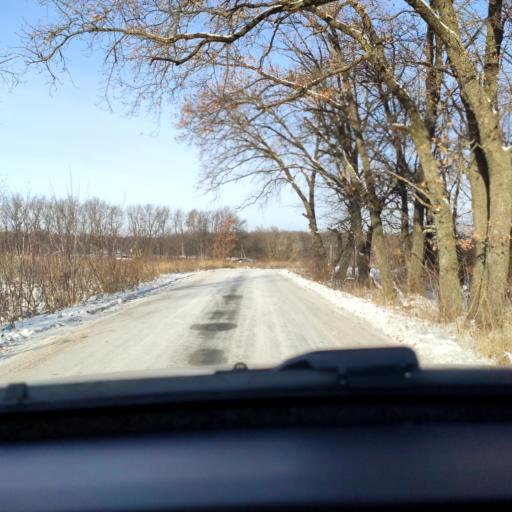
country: RU
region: Voronezj
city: Devitsa
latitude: 51.6037
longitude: 38.9884
